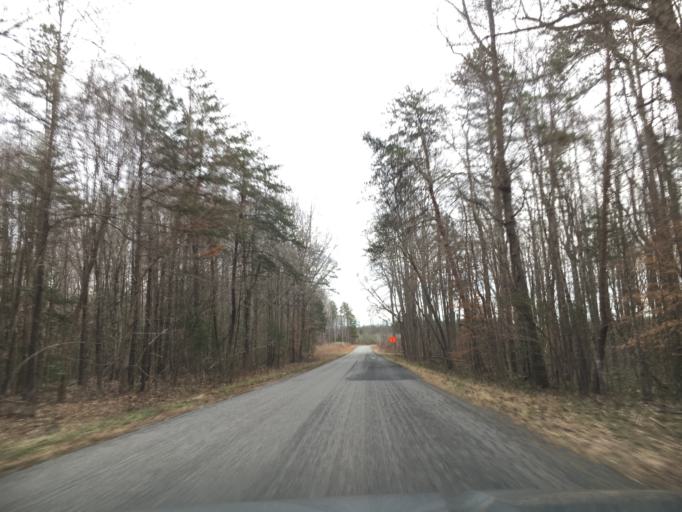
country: US
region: Virginia
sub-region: Amelia County
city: Amelia Court House
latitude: 37.4246
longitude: -77.9972
